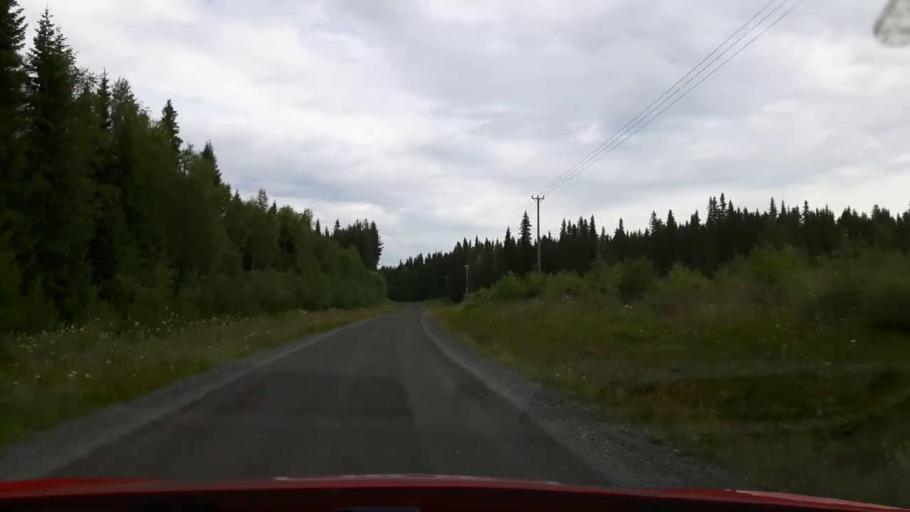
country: SE
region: Jaemtland
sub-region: Stroemsunds Kommun
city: Stroemsund
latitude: 63.4796
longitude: 15.3023
